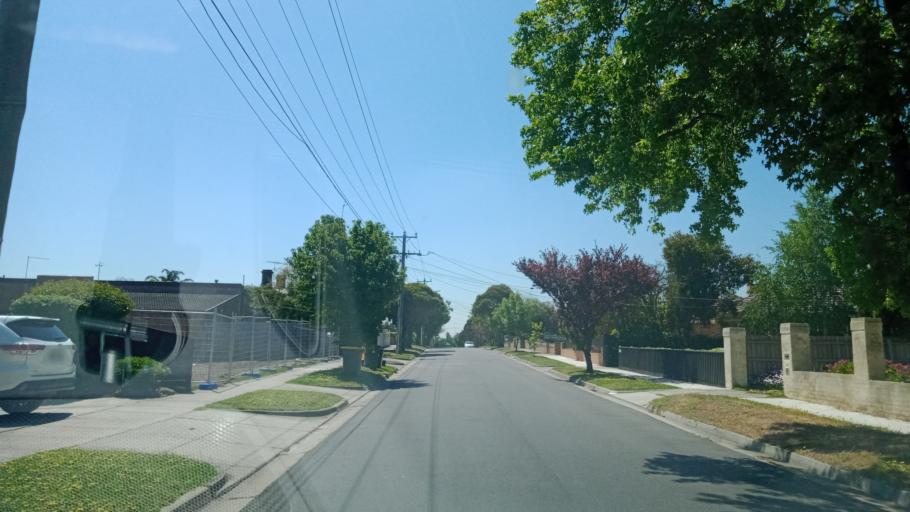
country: AU
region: Victoria
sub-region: Monash
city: Oakleigh South
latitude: -37.9250
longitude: 145.0749
